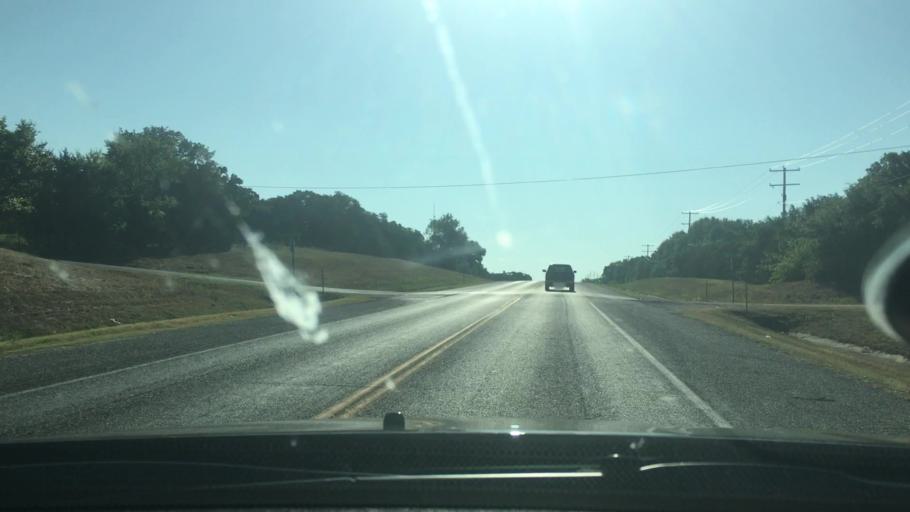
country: US
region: Oklahoma
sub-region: Johnston County
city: Tishomingo
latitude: 34.2369
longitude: -96.7153
